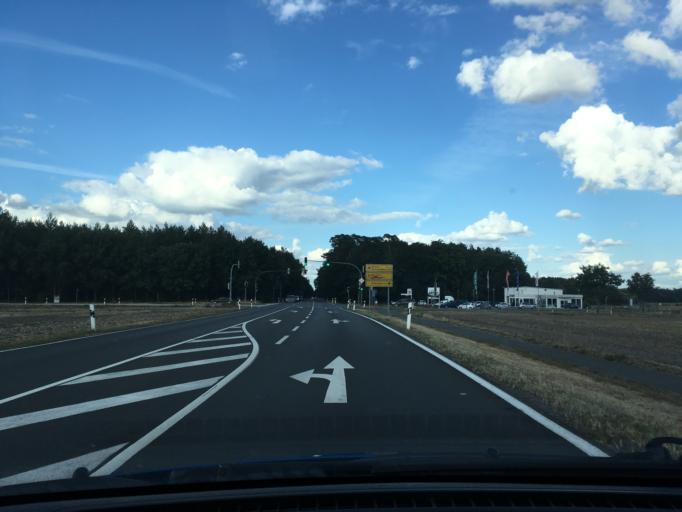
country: DE
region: Mecklenburg-Vorpommern
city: Gross Laasch
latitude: 53.3533
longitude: 11.5374
